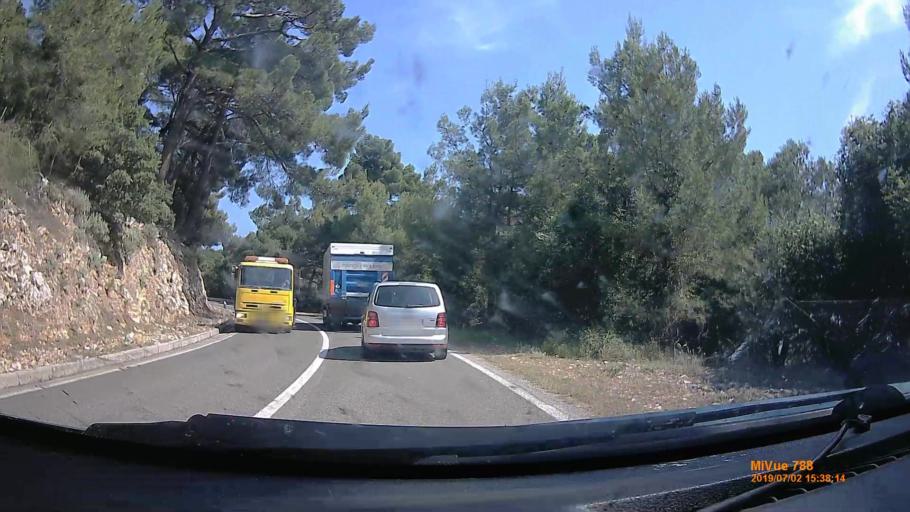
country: HR
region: Primorsko-Goranska
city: Cres
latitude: 44.9751
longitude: 14.4190
